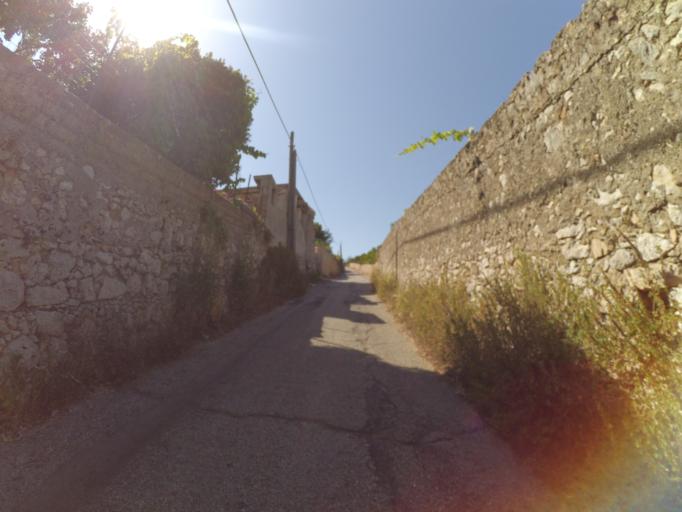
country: IT
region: Latium
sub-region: Provincia di Latina
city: Gaeta
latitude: 41.2195
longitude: 13.5499
